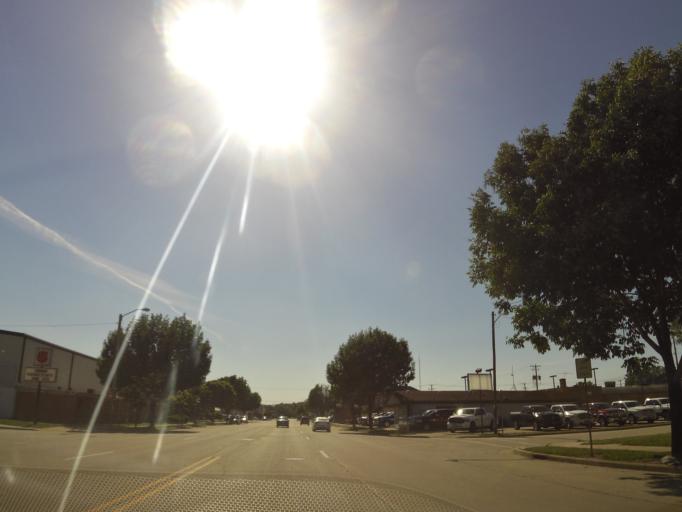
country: US
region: Illinois
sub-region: Winnebago County
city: South Beloit
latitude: 42.4987
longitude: -89.0287
